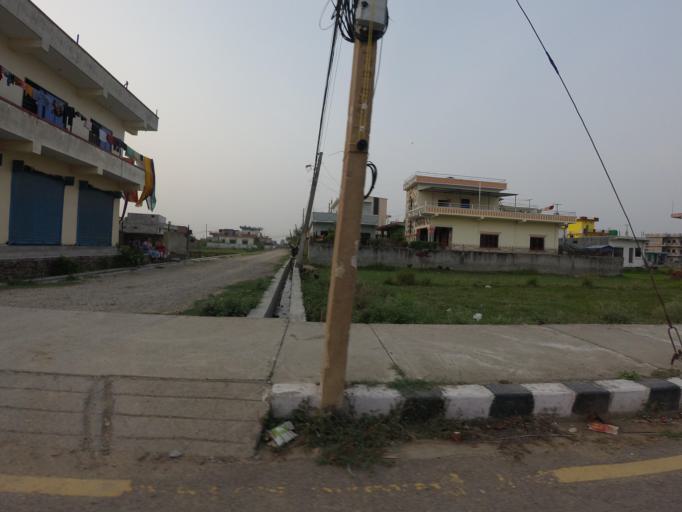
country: NP
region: Western Region
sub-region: Lumbini Zone
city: Bhairahawa
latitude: 27.5132
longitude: 83.4624
